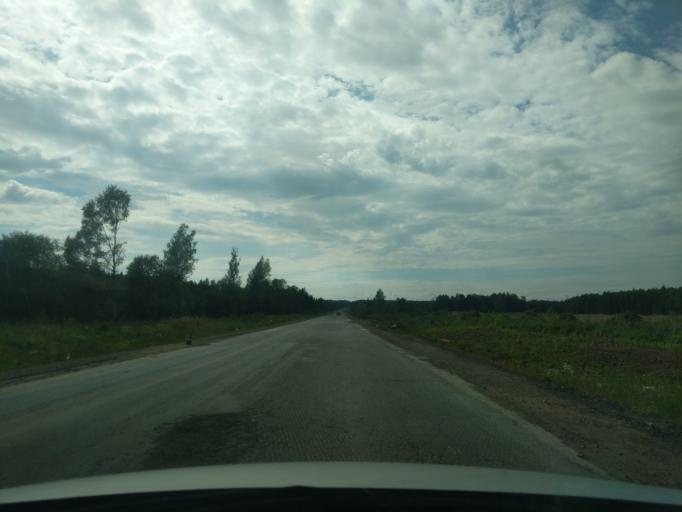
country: RU
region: Kostroma
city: Sudislavl'
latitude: 57.8582
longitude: 41.6105
